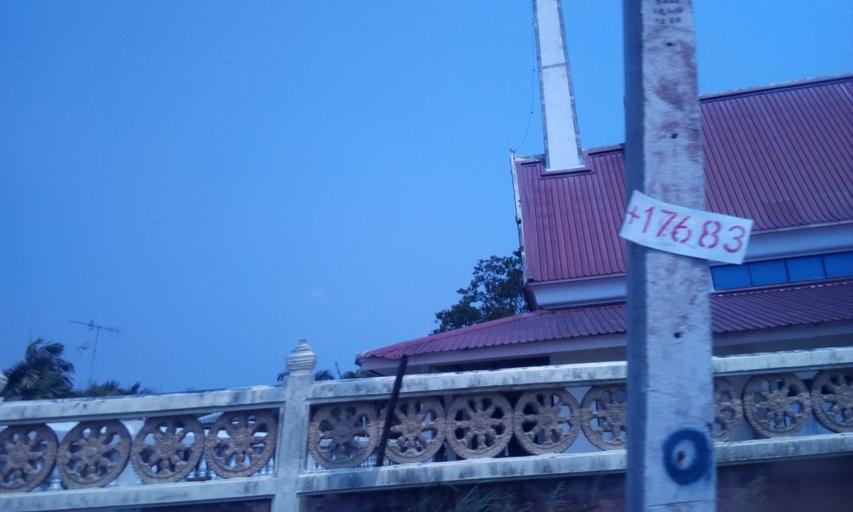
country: TH
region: Chon Buri
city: Phanat Nikhom
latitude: 13.3998
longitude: 101.1904
